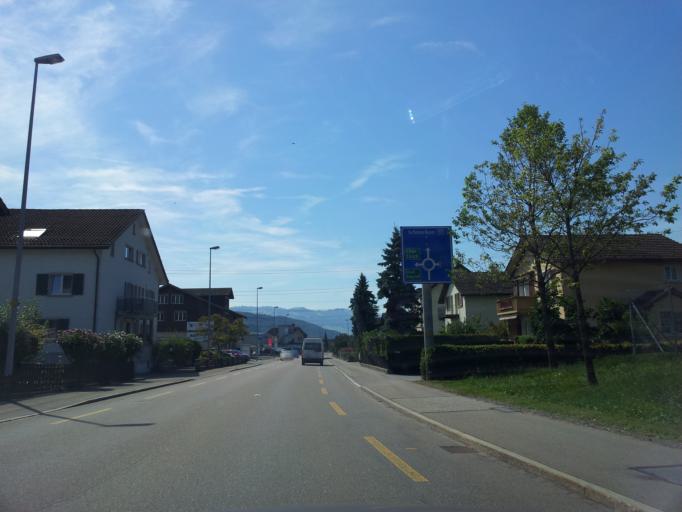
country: CH
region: Saint Gallen
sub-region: Wahlkreis See-Gaster
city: Schmerikon
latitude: 47.2292
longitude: 8.9608
